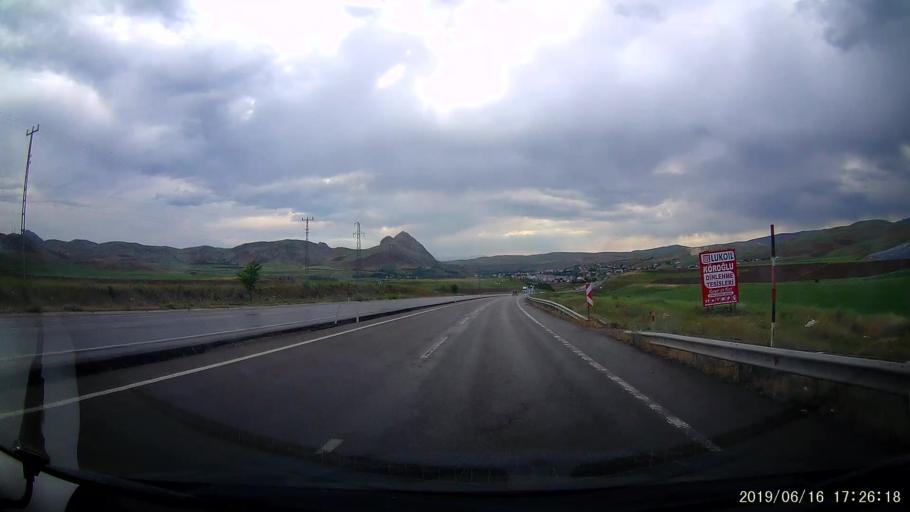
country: TR
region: Erzincan
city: Tercan
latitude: 39.7667
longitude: 40.4156
